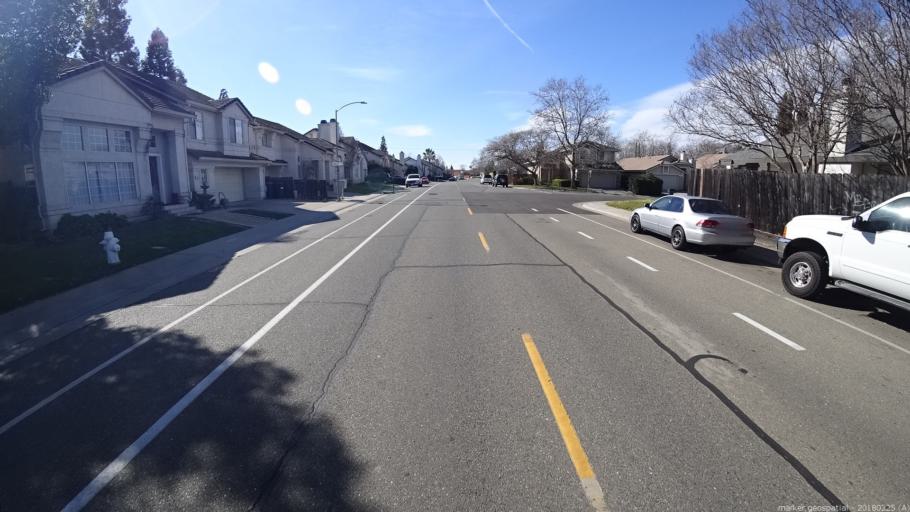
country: US
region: California
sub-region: Sacramento County
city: North Highlands
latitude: 38.7257
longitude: -121.3813
